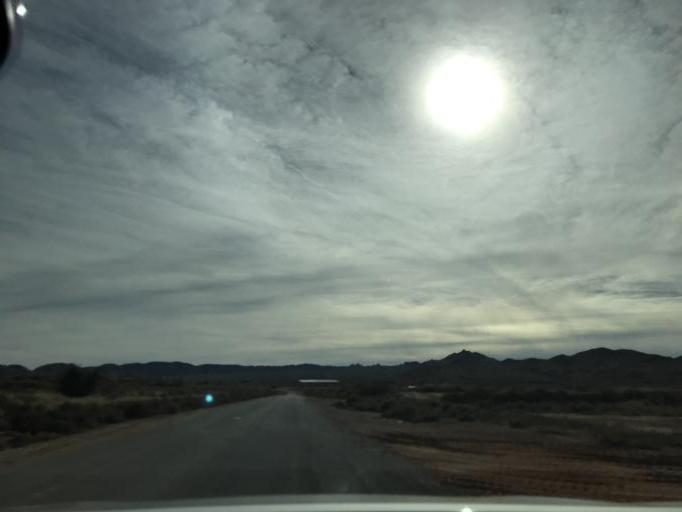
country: US
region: Nevada
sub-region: Clark County
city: Moapa Town
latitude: 36.6642
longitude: -114.5619
